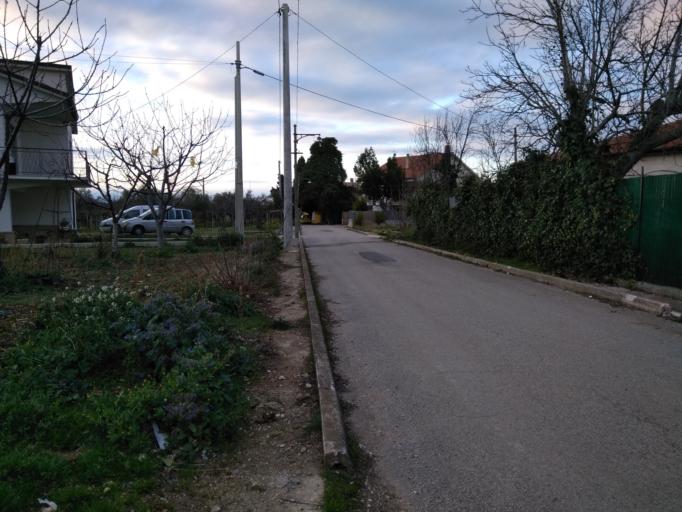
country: IT
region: Abruzzo
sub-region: Provincia di Chieti
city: Poggiofiorito
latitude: 42.2598
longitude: 14.3204
